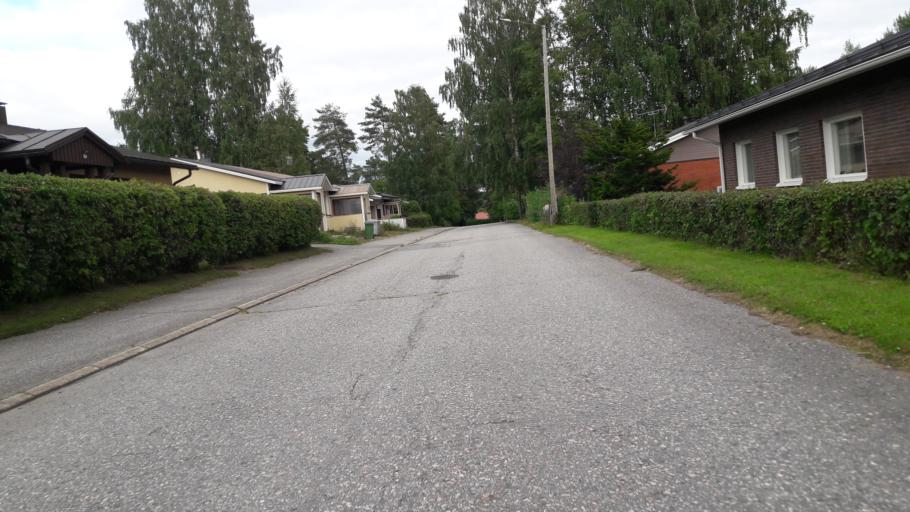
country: FI
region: North Karelia
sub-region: Joensuu
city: Joensuu
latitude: 62.5816
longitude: 29.8003
